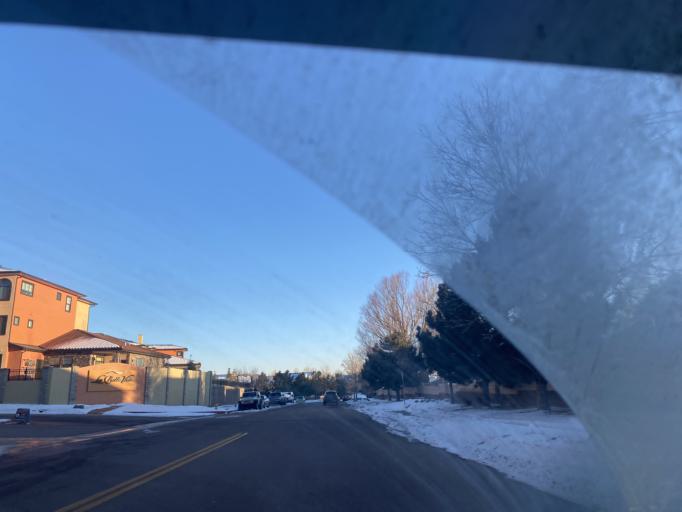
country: US
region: Colorado
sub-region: El Paso County
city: Black Forest
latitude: 38.9655
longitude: -104.7451
